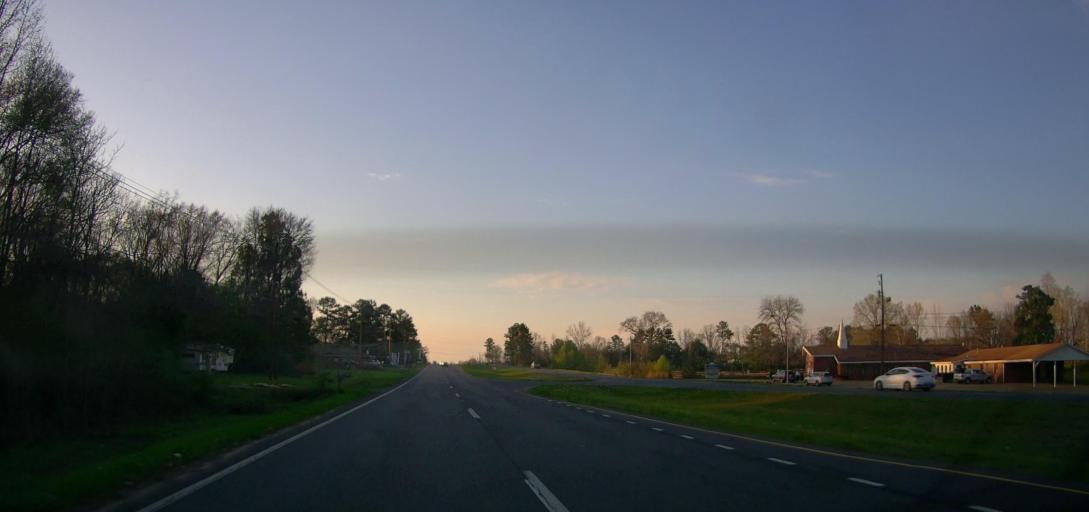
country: US
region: Alabama
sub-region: Talladega County
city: Childersburg
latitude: 33.2522
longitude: -86.3420
